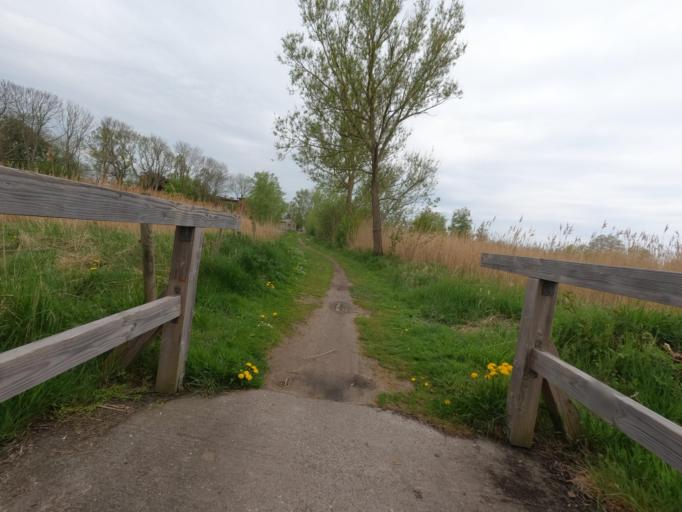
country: DE
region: Mecklenburg-Vorpommern
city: Saal
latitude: 54.3337
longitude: 12.5281
